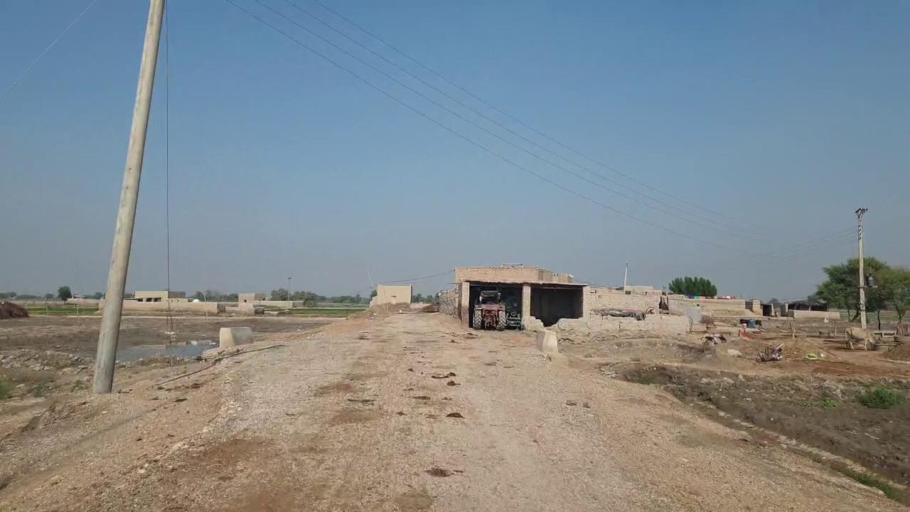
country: PK
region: Sindh
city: Sehwan
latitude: 26.4244
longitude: 67.8103
